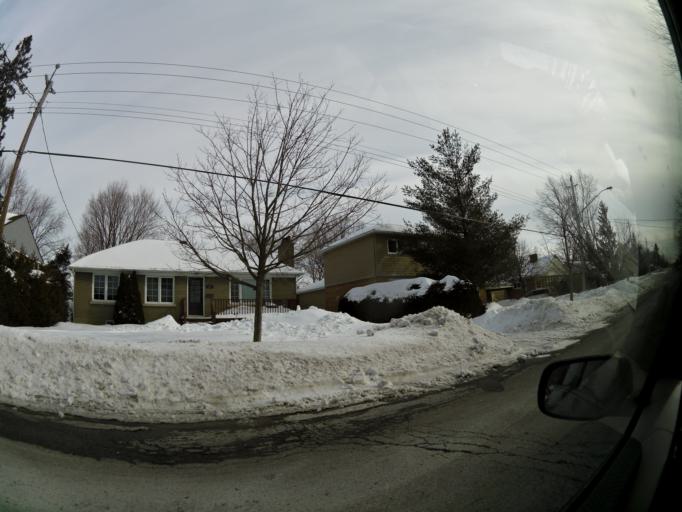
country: CA
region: Ontario
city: Ottawa
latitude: 45.4431
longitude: -75.6083
